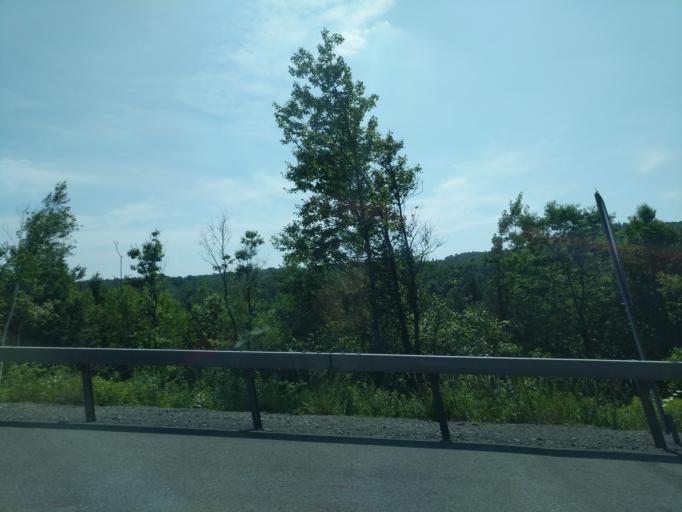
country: US
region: New York
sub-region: Sullivan County
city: Liberty
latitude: 41.8376
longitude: -74.7437
